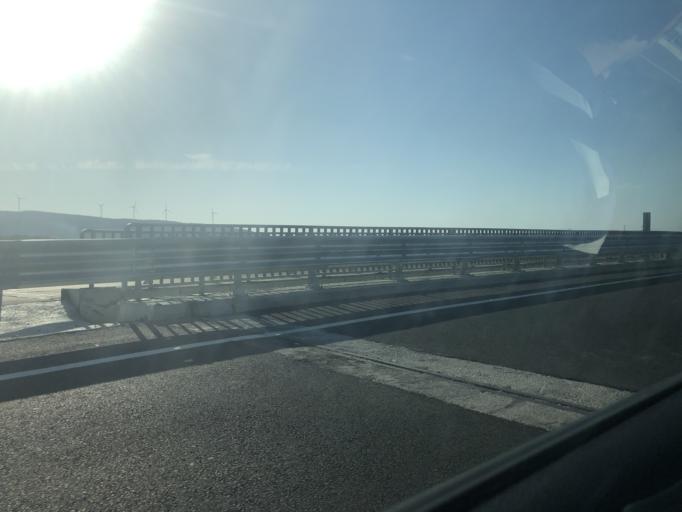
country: TR
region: Istanbul
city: Catalca
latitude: 41.1621
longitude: 28.4625
